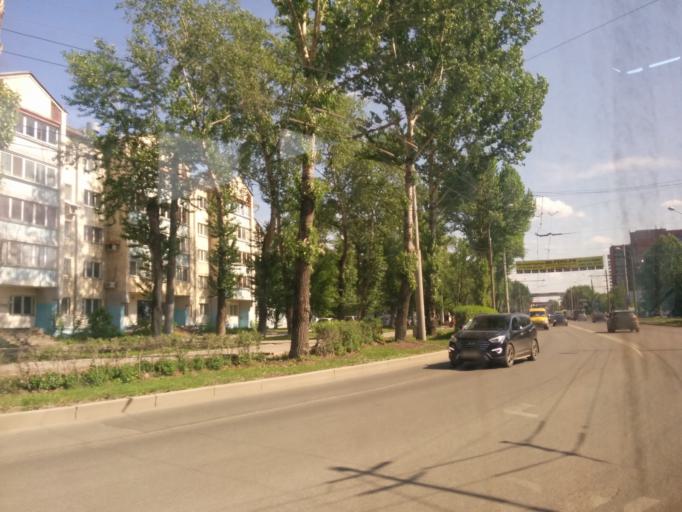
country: RU
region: Perm
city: Perm
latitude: 58.0119
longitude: 56.2798
